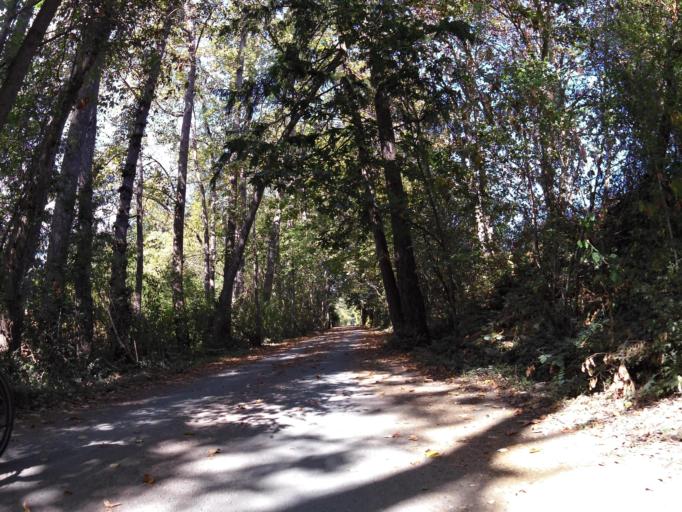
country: CA
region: British Columbia
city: Victoria
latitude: 48.5381
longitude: -123.3798
